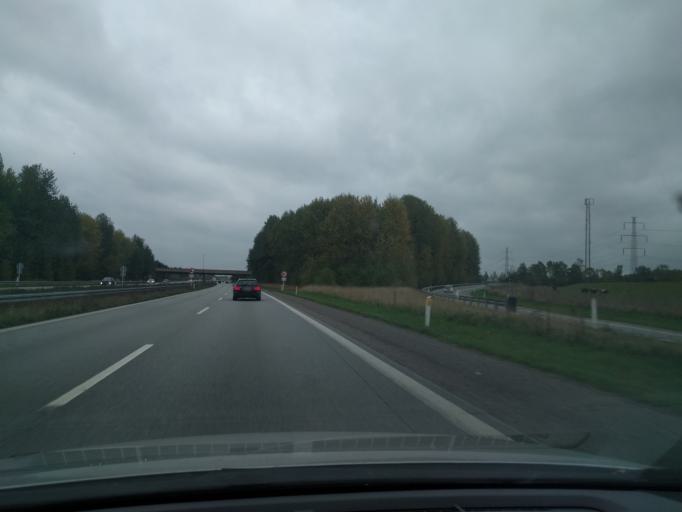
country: DK
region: Zealand
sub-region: Ringsted Kommune
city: Ringsted
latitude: 55.4559
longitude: 11.8197
